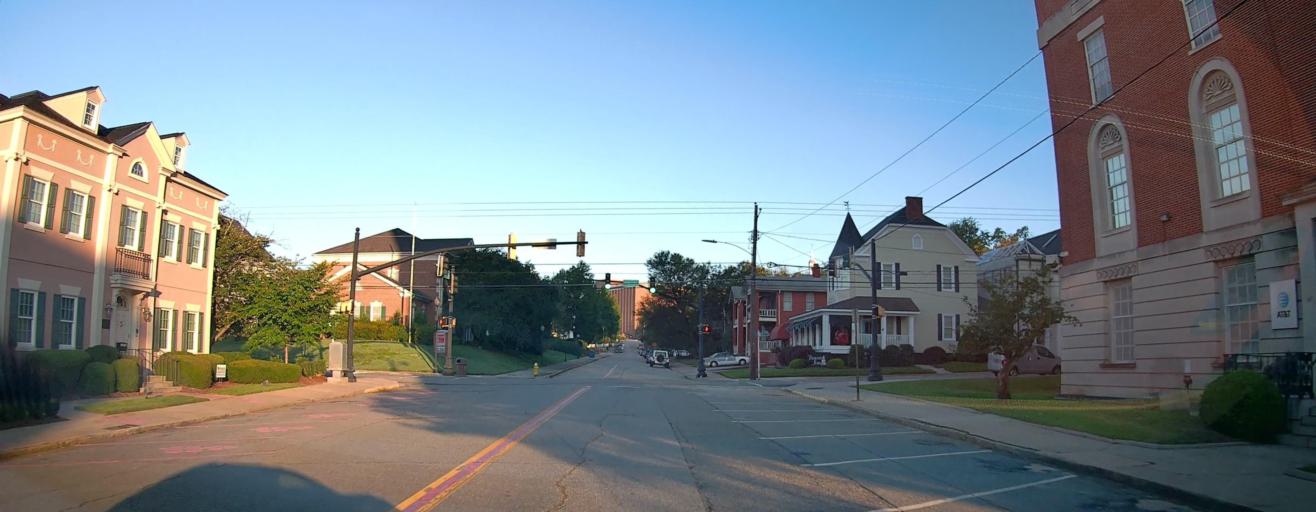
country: US
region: Georgia
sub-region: Bibb County
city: Macon
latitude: 32.8382
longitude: -83.6317
